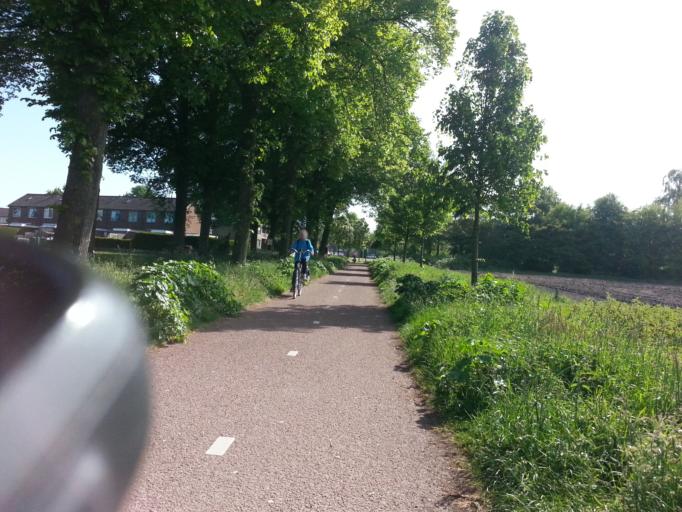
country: NL
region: Gelderland
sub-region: Berkelland
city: Eibergen
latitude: 52.0981
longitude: 6.6335
